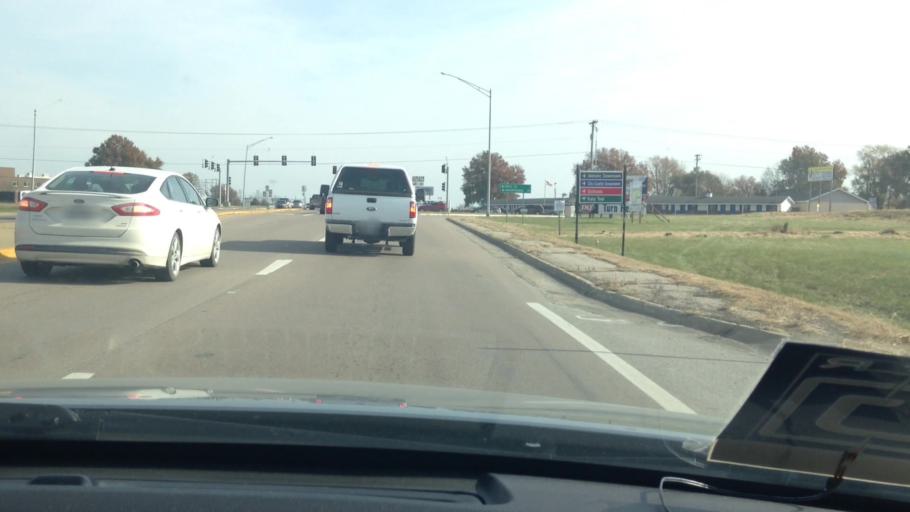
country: US
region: Missouri
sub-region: Henry County
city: Clinton
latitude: 38.3883
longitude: -93.7729
